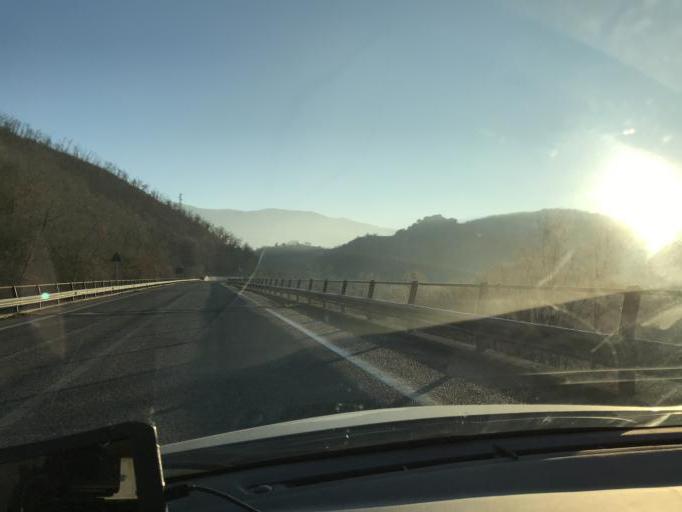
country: IT
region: Latium
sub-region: Provincia di Rieti
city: Concerviano
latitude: 42.3318
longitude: 12.9841
